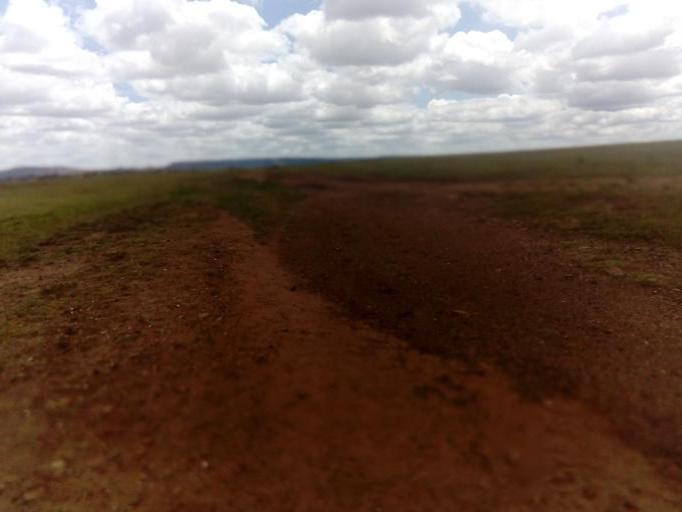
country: LS
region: Berea
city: Teyateyaneng
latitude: -29.1235
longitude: 27.7607
